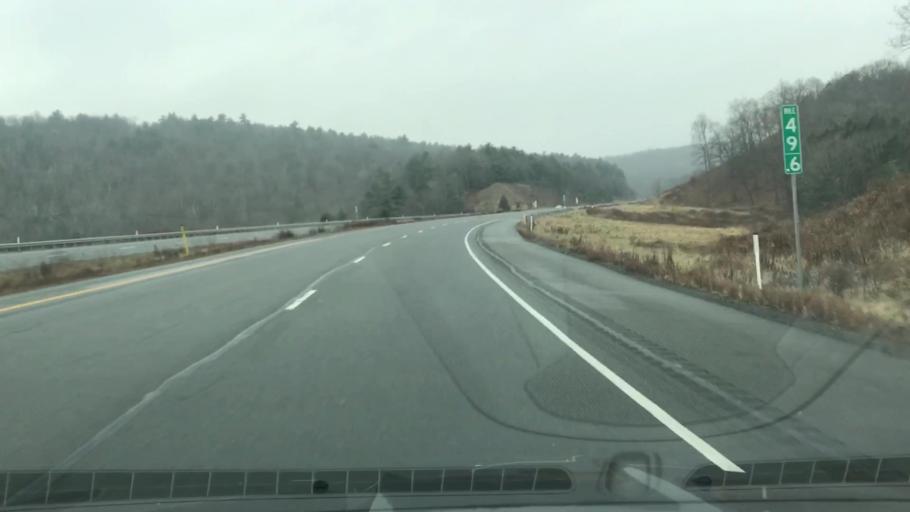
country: US
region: Pennsylvania
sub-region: Pike County
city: Milford
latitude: 41.3408
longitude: -74.7790
